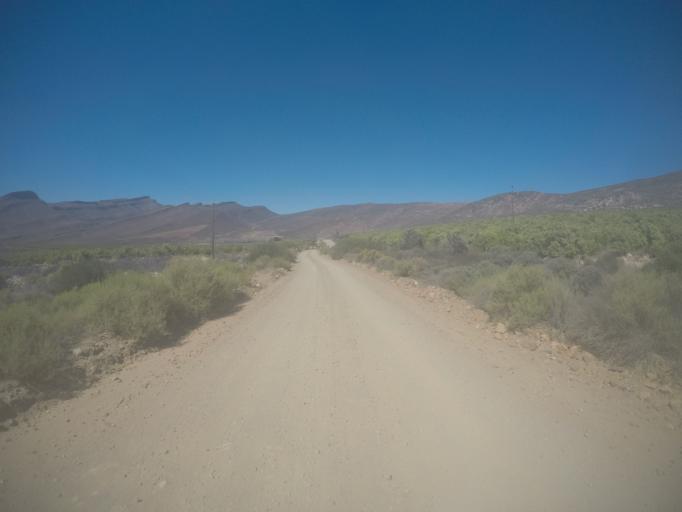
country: ZA
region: Western Cape
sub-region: West Coast District Municipality
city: Clanwilliam
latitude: -32.5562
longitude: 19.3616
